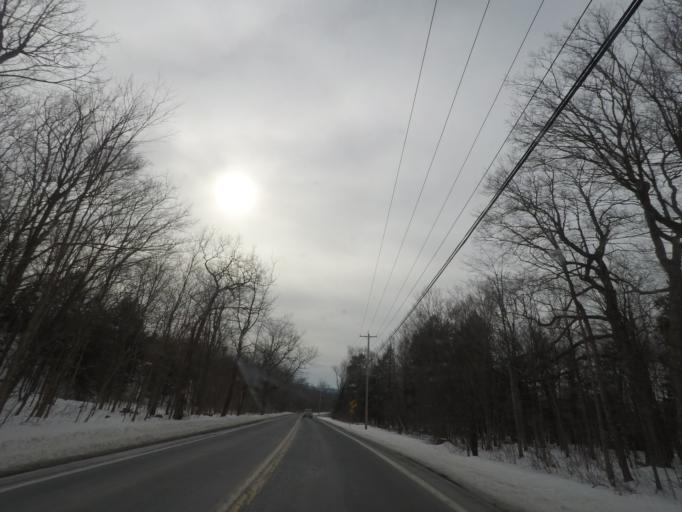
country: US
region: New York
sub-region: Albany County
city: Altamont
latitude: 42.6807
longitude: -74.0929
